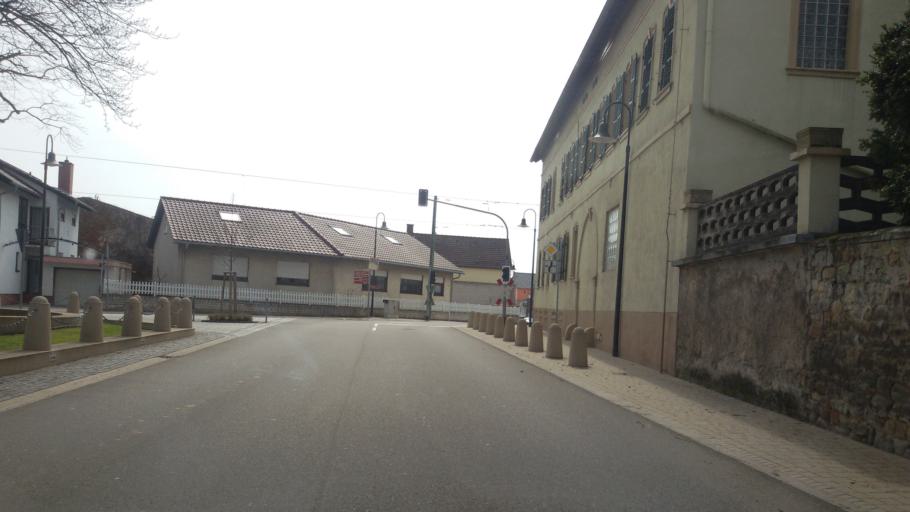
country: DE
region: Rheinland-Pfalz
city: Ellerstadt
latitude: 49.4634
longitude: 8.2583
